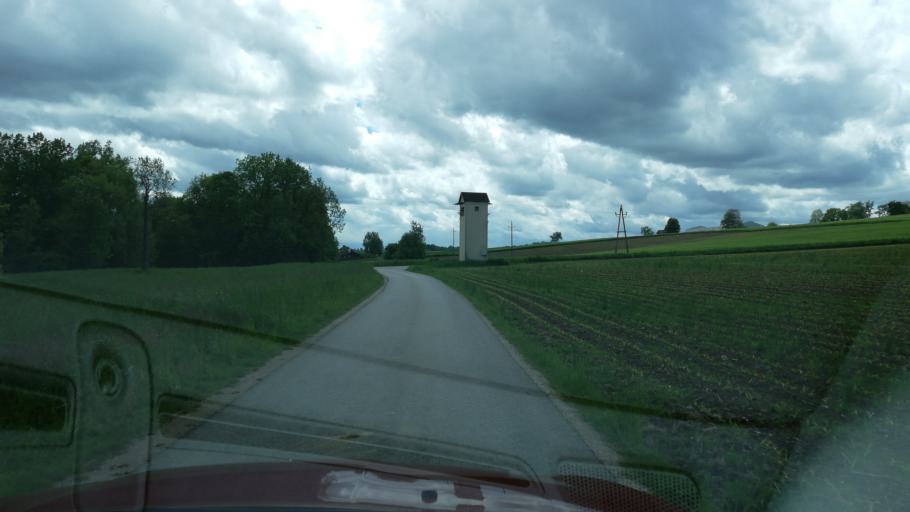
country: AT
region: Upper Austria
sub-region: Politischer Bezirk Linz-Land
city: Horsching
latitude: 48.1784
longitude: 14.1986
